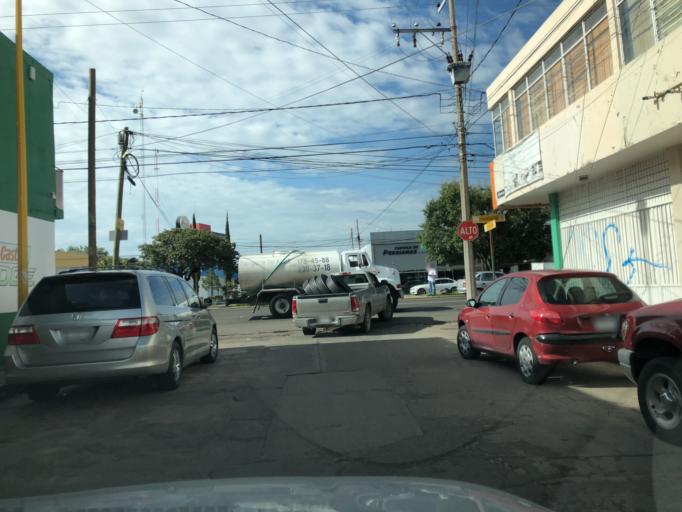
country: MX
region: Aguascalientes
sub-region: Aguascalientes
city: Aguascalientes
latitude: 21.8676
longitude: -102.3052
